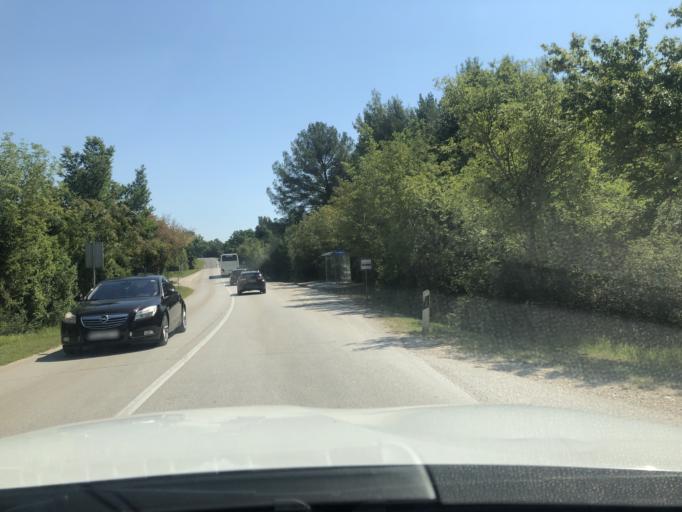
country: HR
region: Istarska
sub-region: Grad Rovinj
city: Rovinj
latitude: 45.0523
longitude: 13.7167
